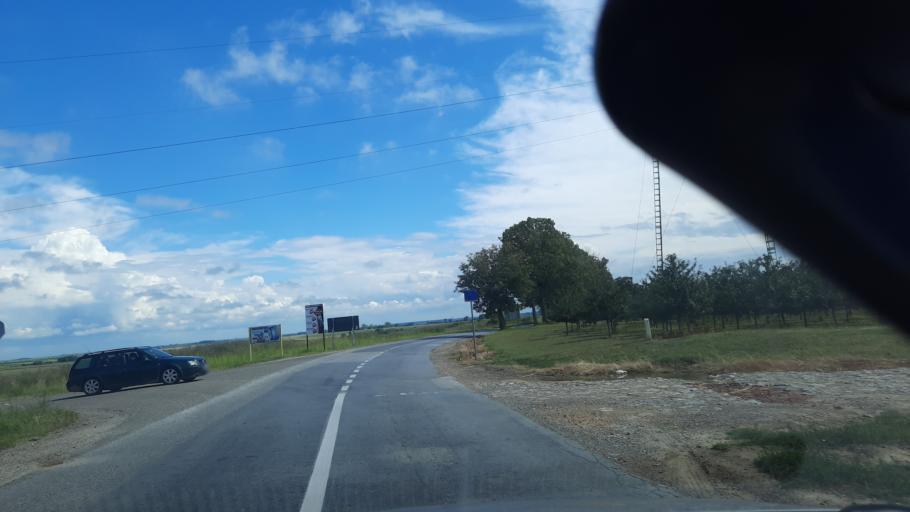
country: RS
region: Autonomna Pokrajina Vojvodina
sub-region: Sremski Okrug
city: Sremska Mitrovica
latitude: 45.0688
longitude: 19.5947
